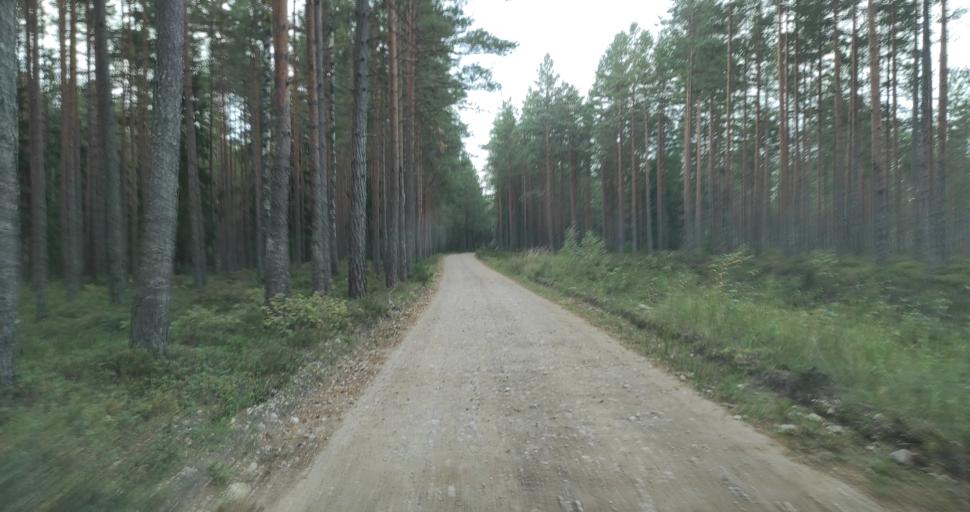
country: LV
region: Kuldigas Rajons
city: Kuldiga
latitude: 57.2307
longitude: 22.0915
